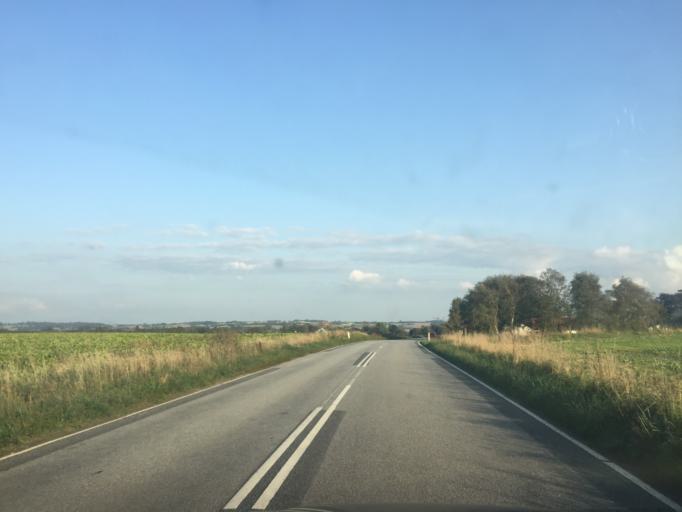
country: DK
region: Zealand
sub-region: Kalundborg Kommune
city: Svebolle
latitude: 55.6005
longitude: 11.2766
